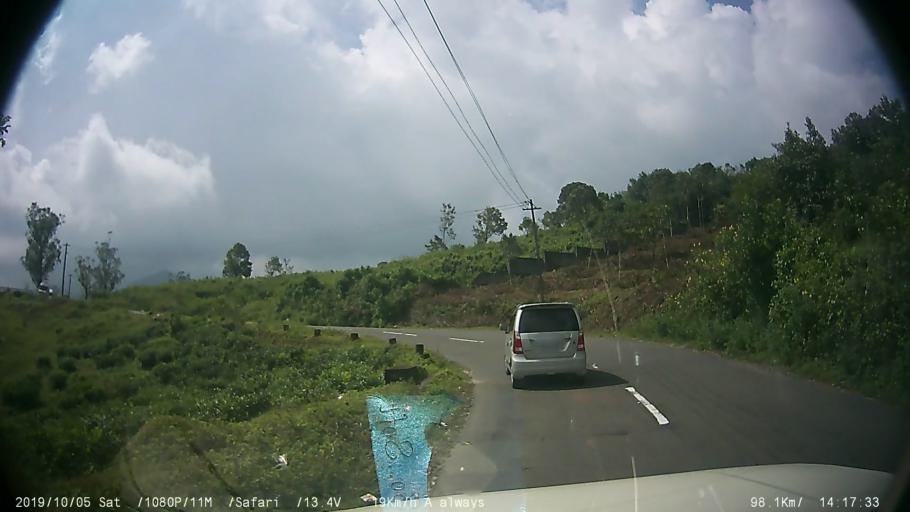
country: IN
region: Kerala
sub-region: Kottayam
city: Erattupetta
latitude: 9.5861
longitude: 76.9691
